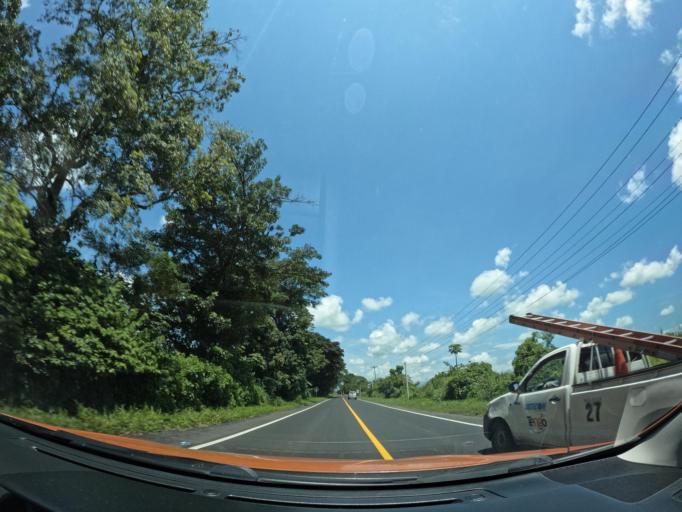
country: GT
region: Escuintla
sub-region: Municipio de Masagua
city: Masagua
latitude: 14.1886
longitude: -90.8591
